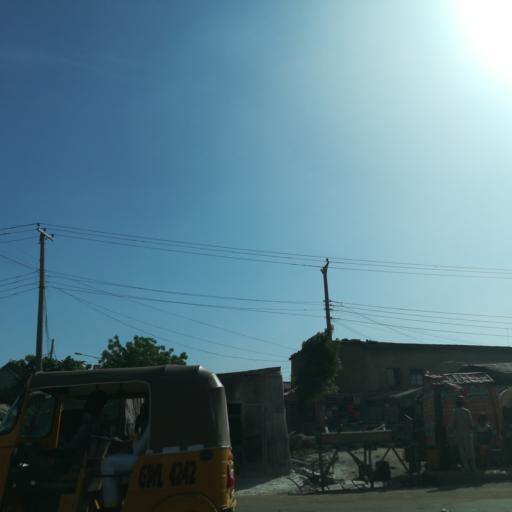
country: NG
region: Kano
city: Kano
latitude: 12.0152
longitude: 8.5176
